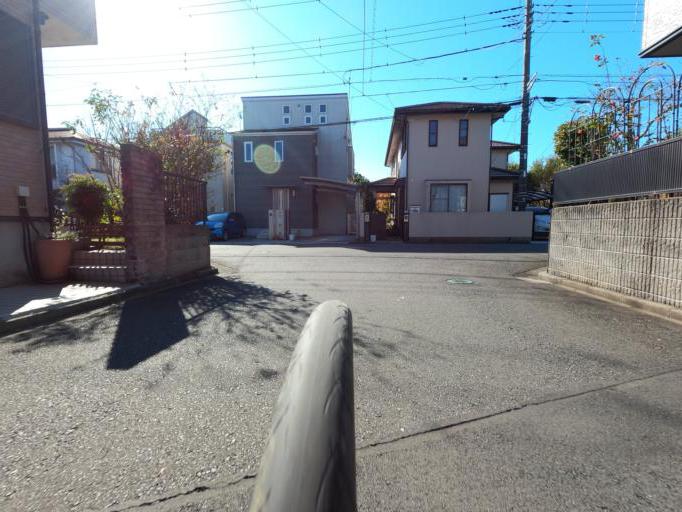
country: JP
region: Ibaraki
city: Moriya
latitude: 35.9413
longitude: 139.9847
